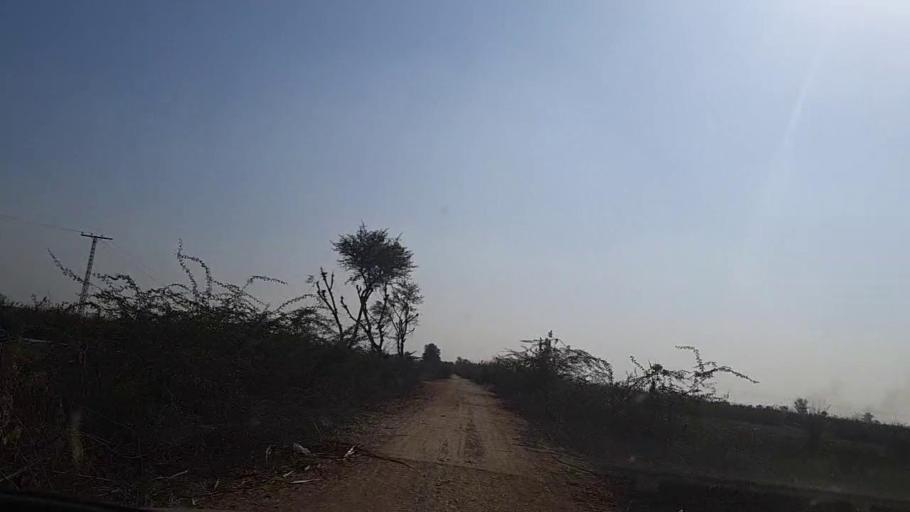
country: PK
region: Sindh
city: Sakrand
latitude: 26.0796
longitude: 68.3694
